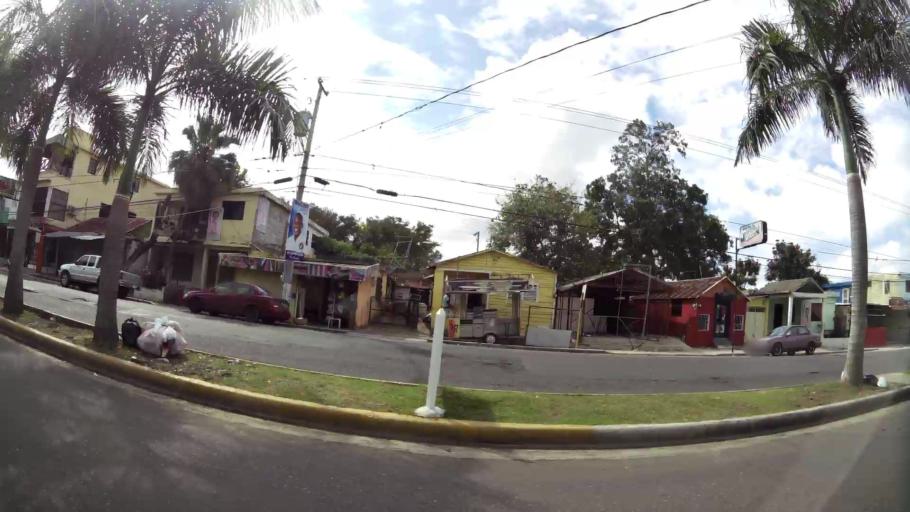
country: DO
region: Santiago
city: Santiago de los Caballeros
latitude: 19.4629
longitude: -70.6753
